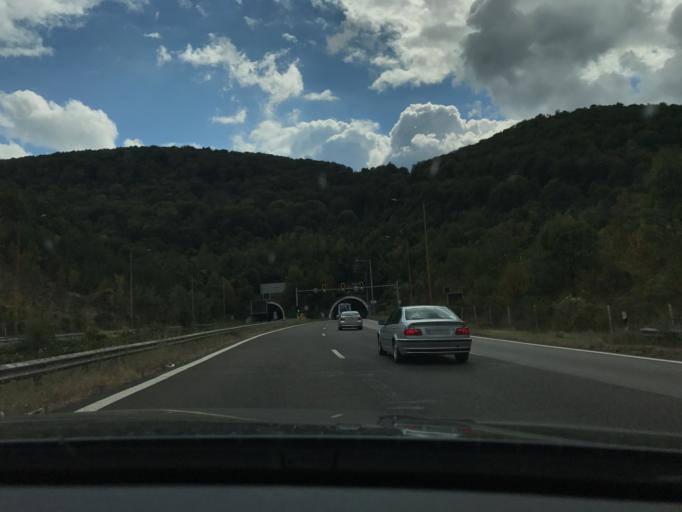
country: BG
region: Sofiya
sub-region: Obshtina Botevgrad
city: Botevgrad
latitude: 42.8439
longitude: 23.7967
